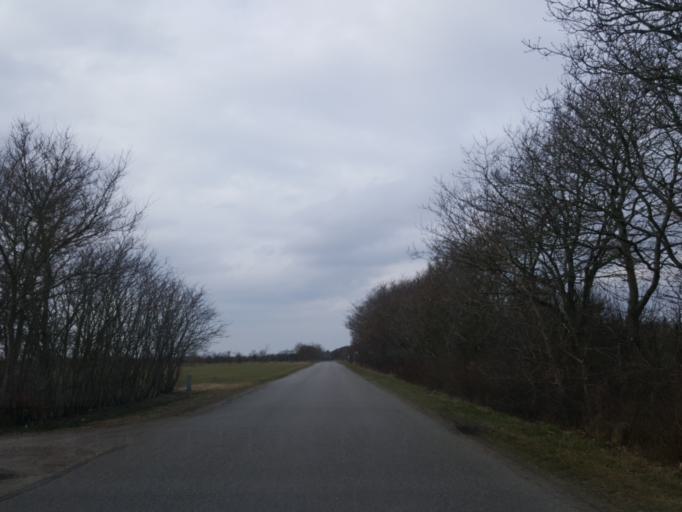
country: DK
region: Central Jutland
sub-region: Holstebro Kommune
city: Ulfborg
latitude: 56.3646
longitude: 8.2472
